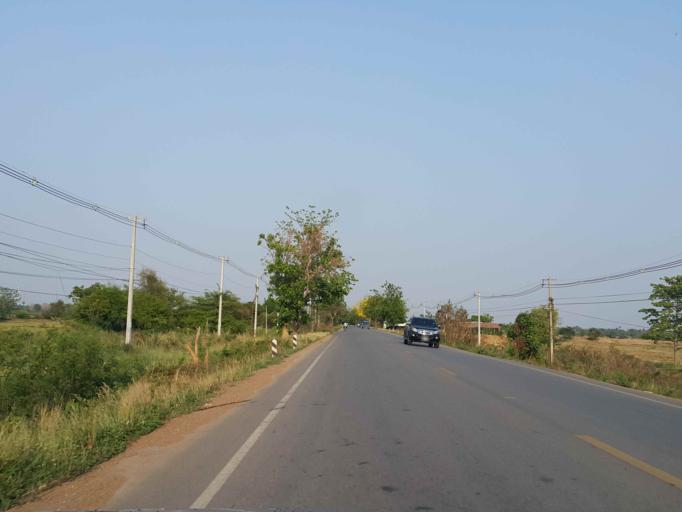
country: TH
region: Sukhothai
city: Sawankhalok
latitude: 17.3101
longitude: 99.8048
